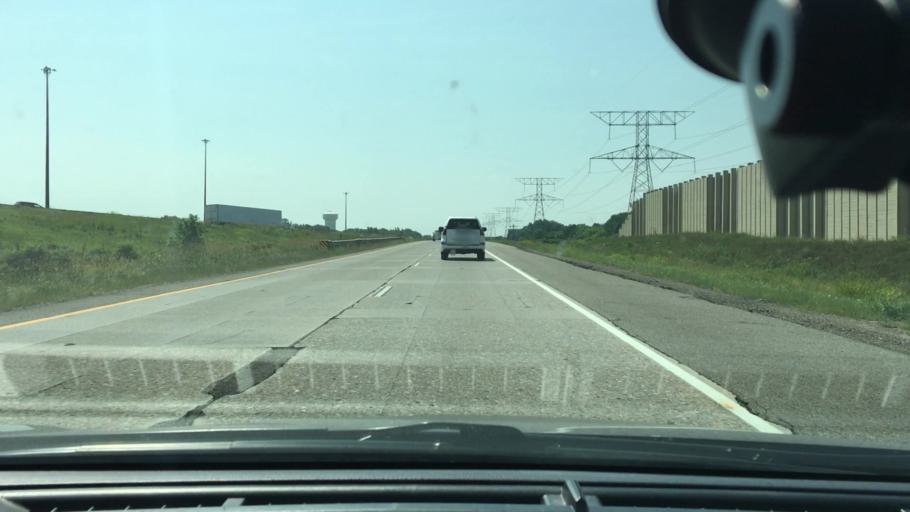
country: US
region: Minnesota
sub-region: Hennepin County
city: Maple Grove
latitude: 45.0917
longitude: -93.4480
